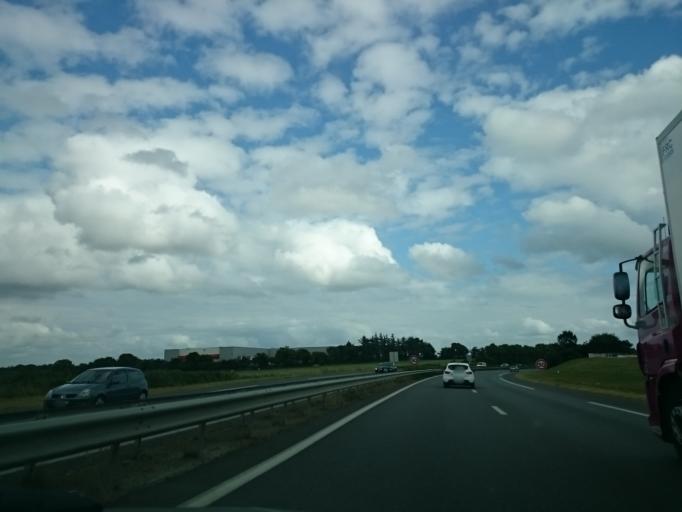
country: FR
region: Brittany
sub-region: Departement du Finistere
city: Gouesnou
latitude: 48.4294
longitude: -4.4385
